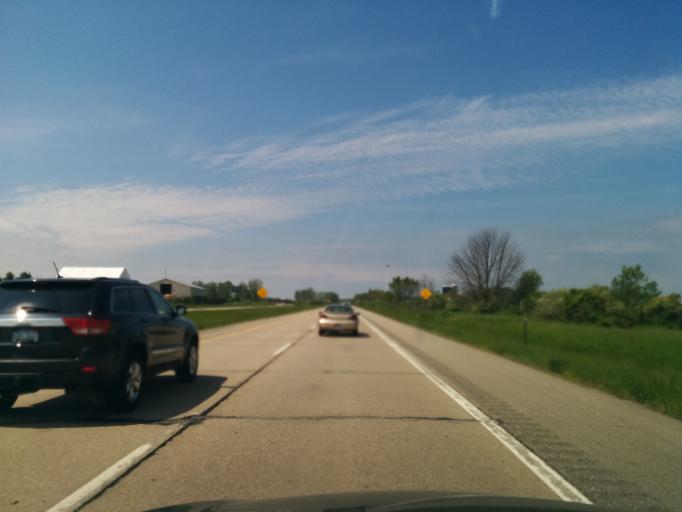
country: US
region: Michigan
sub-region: Ottawa County
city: Holland
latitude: 42.7387
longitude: -86.1375
